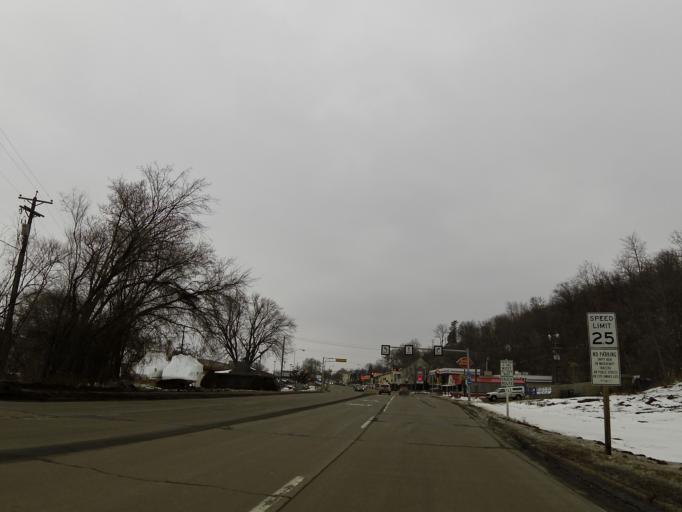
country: US
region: Wisconsin
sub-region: Saint Croix County
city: Hudson
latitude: 44.9699
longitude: -92.7566
